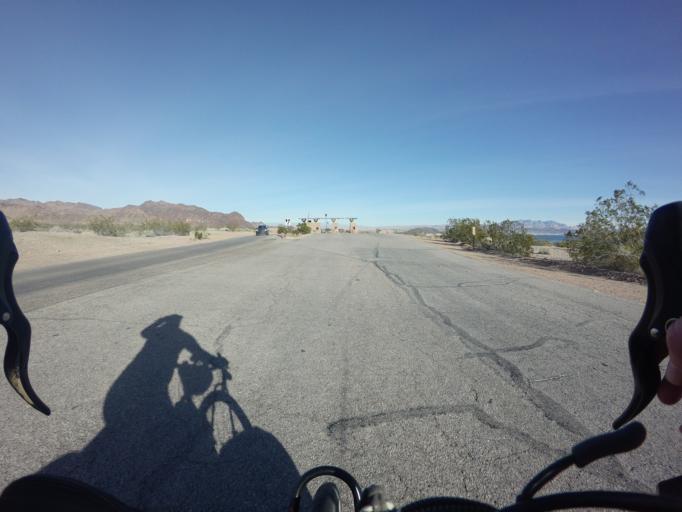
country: US
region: Nevada
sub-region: Clark County
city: Boulder City
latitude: 36.0198
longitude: -114.7956
